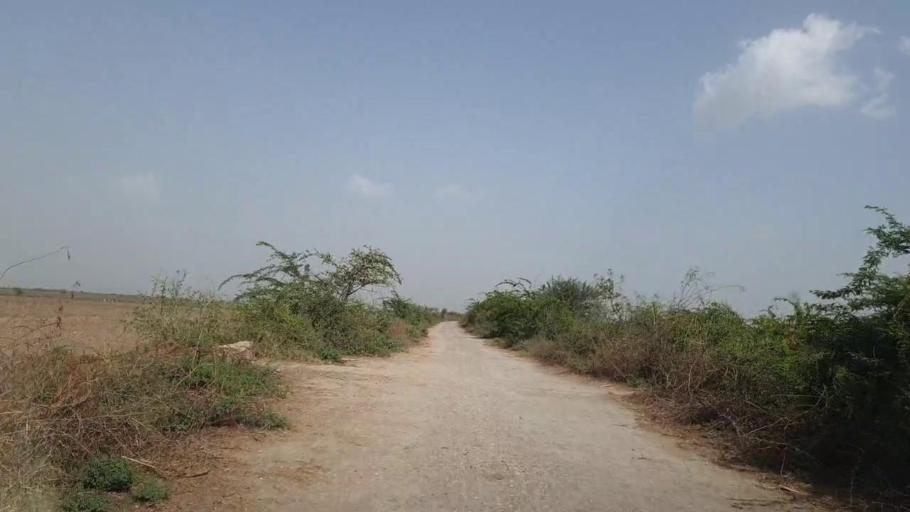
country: PK
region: Sindh
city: Rajo Khanani
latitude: 25.0326
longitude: 68.8731
